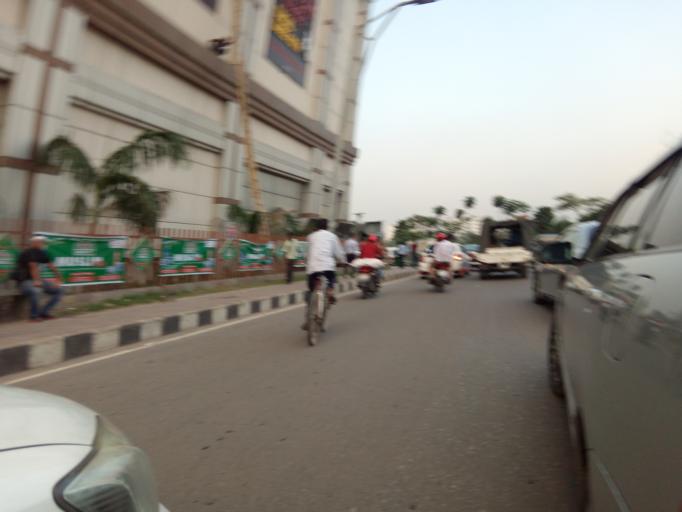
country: BD
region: Dhaka
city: Paltan
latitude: 23.7726
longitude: 90.4161
